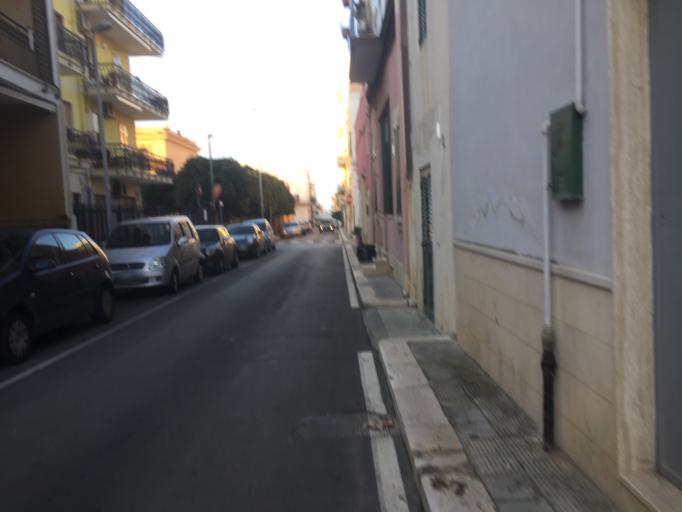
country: IT
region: Apulia
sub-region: Provincia di Bari
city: Parco Scizzo-Parchitello
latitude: 41.0860
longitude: 16.9990
